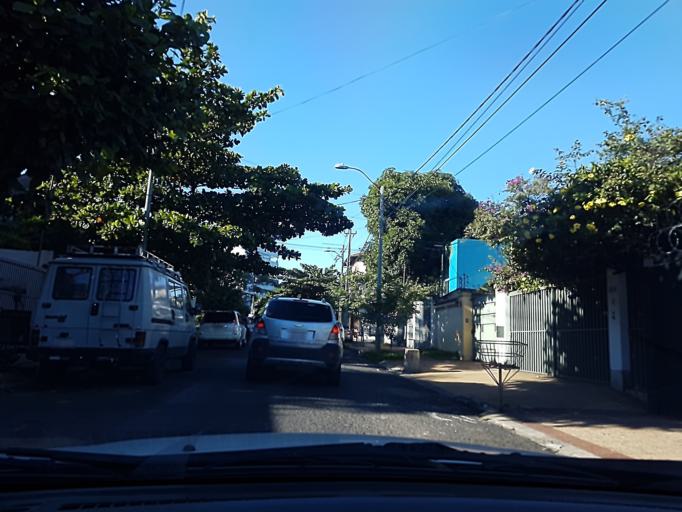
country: PY
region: Asuncion
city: Asuncion
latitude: -25.2832
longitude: -57.6027
